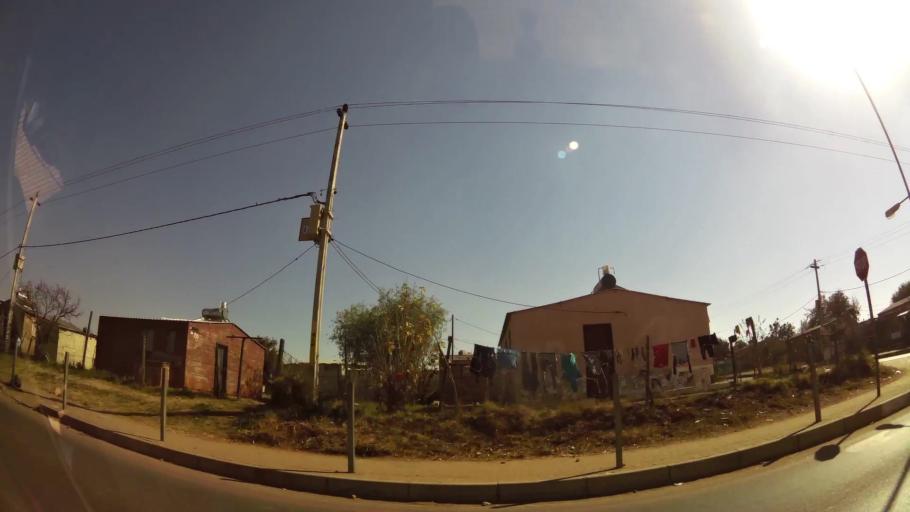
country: ZA
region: Gauteng
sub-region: City of Johannesburg Metropolitan Municipality
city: Johannesburg
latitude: -26.1839
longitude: 27.9646
